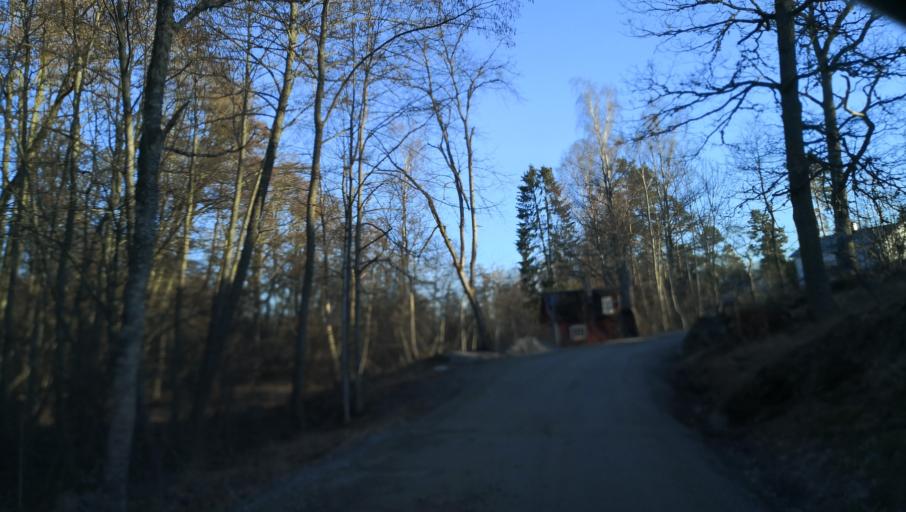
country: SE
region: Stockholm
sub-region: Varmdo Kommun
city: Mortnas
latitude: 59.3310
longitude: 18.4347
